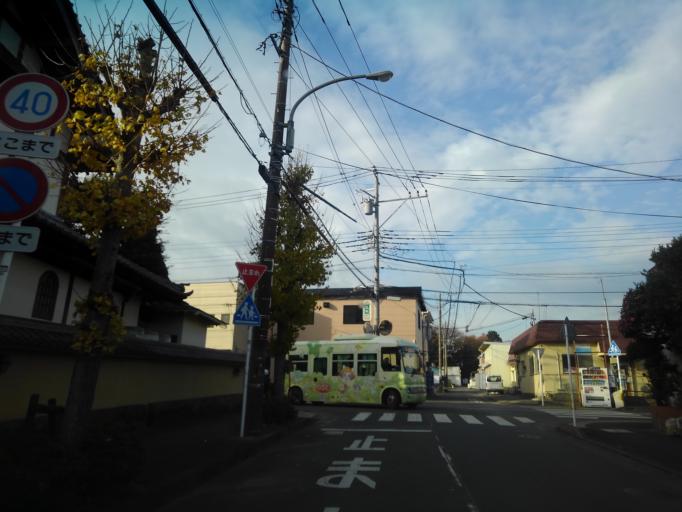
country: JP
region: Tokyo
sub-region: Machida-shi
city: Machida
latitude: 35.5149
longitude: 139.4516
